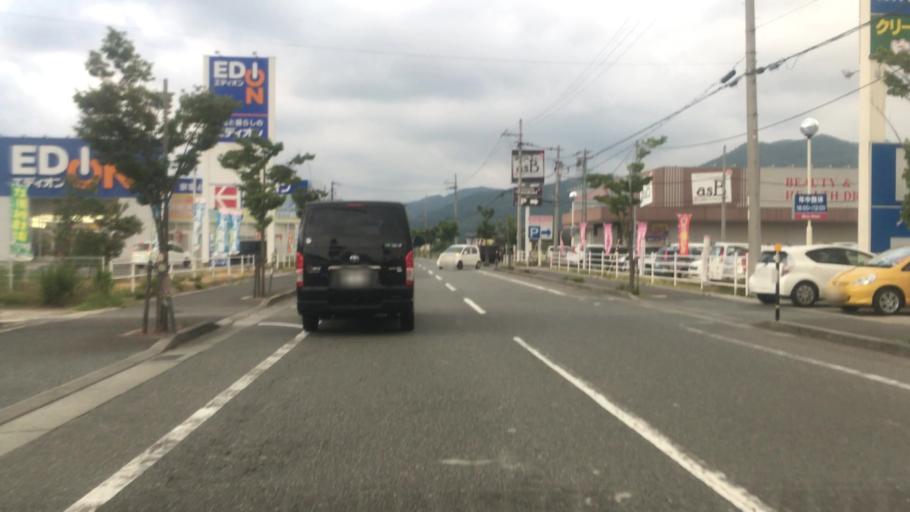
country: JP
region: Hyogo
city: Toyooka
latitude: 35.5551
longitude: 134.8155
